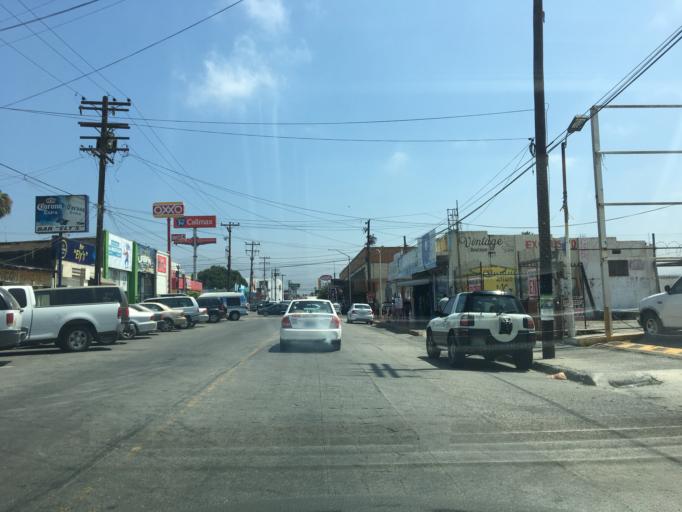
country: MX
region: Baja California
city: Ensenada
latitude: 31.8642
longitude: -116.6277
